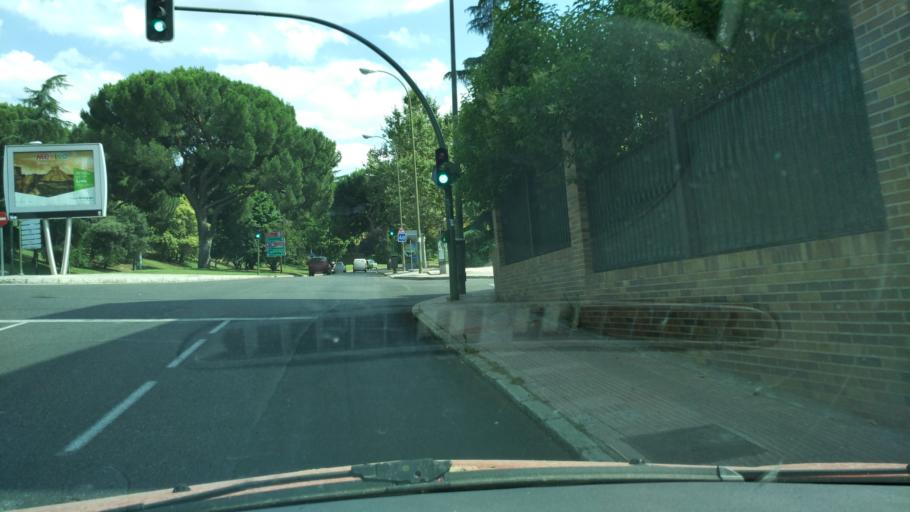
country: ES
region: Madrid
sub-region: Provincia de Madrid
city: Tetuan de las Victorias
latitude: 40.4625
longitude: -3.7197
